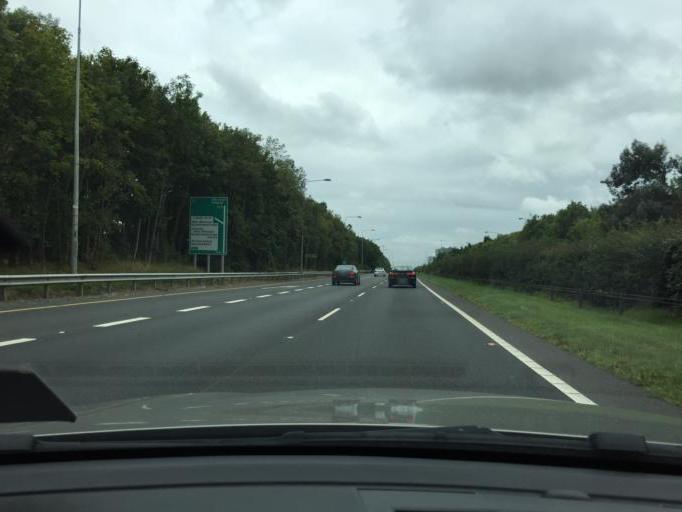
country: IE
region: Leinster
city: Hartstown
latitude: 53.4029
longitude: -6.4019
